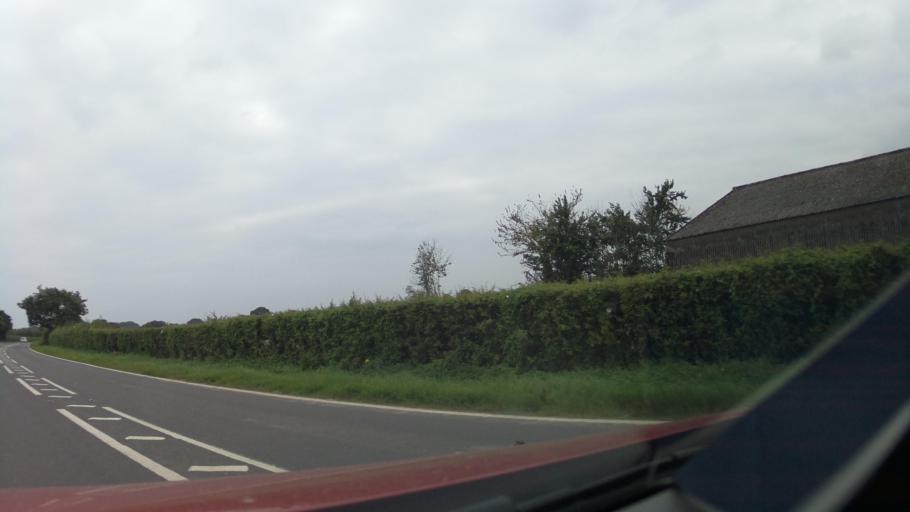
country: GB
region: England
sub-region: Shropshire
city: Shawbury
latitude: 52.7790
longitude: -2.6635
